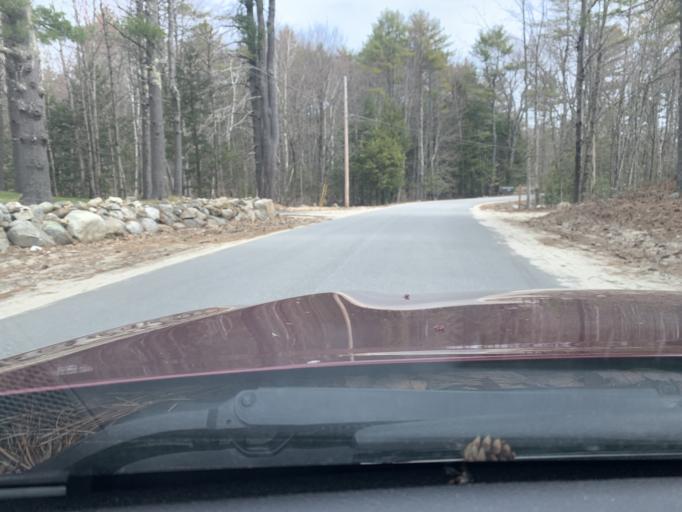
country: US
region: Maine
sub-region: Androscoggin County
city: Poland
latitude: 43.9658
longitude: -70.3875
